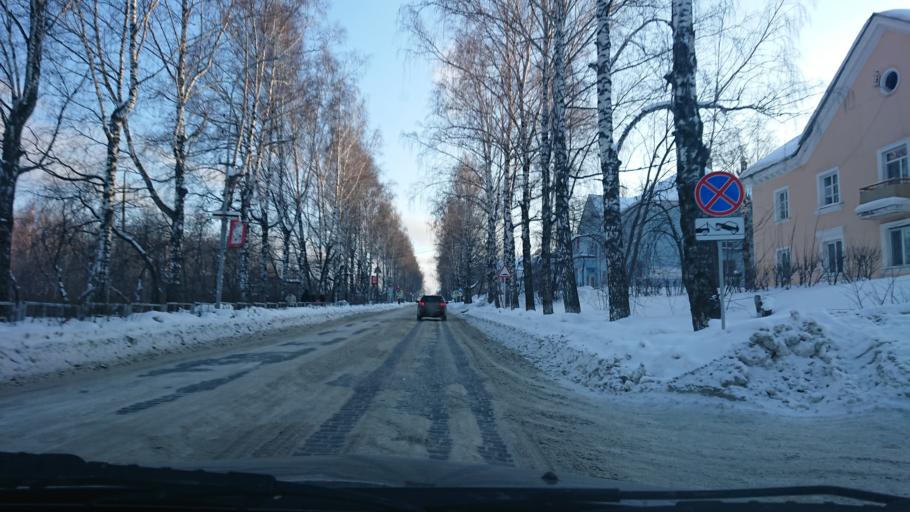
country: RU
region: Sverdlovsk
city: Degtyarsk
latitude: 56.6965
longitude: 60.0881
